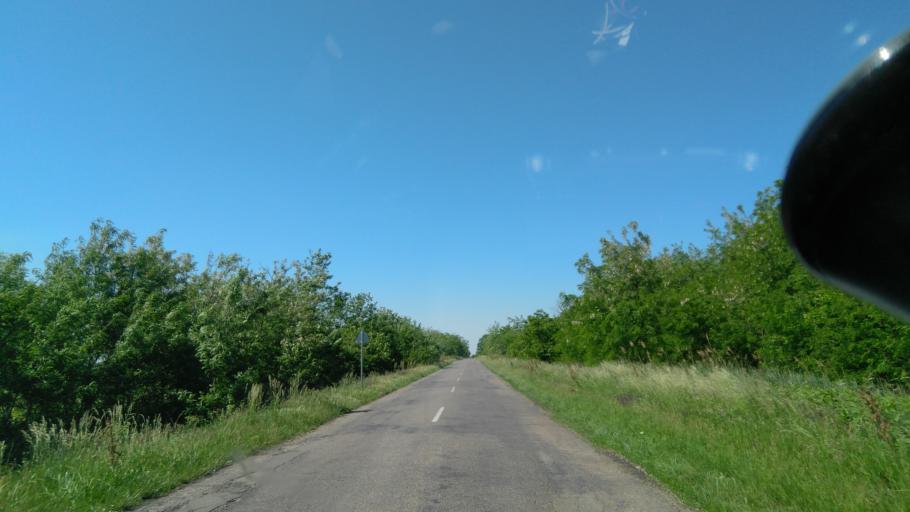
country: HU
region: Bekes
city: Kunagota
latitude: 46.4232
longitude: 21.0748
